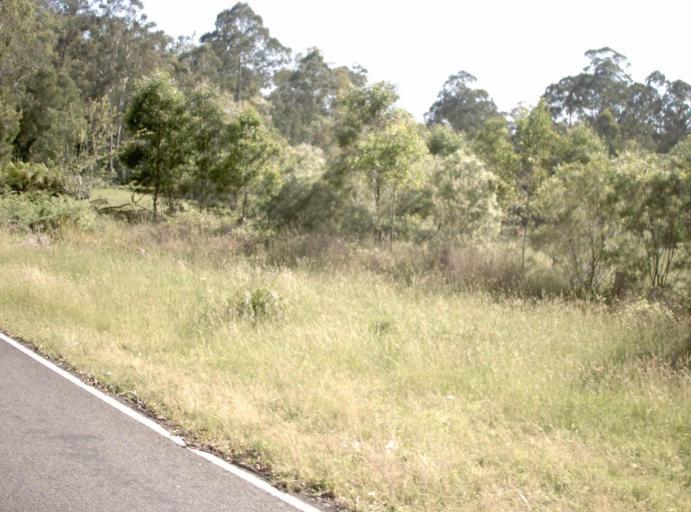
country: AU
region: New South Wales
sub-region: Bombala
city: Bombala
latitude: -37.3674
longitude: 148.6824
